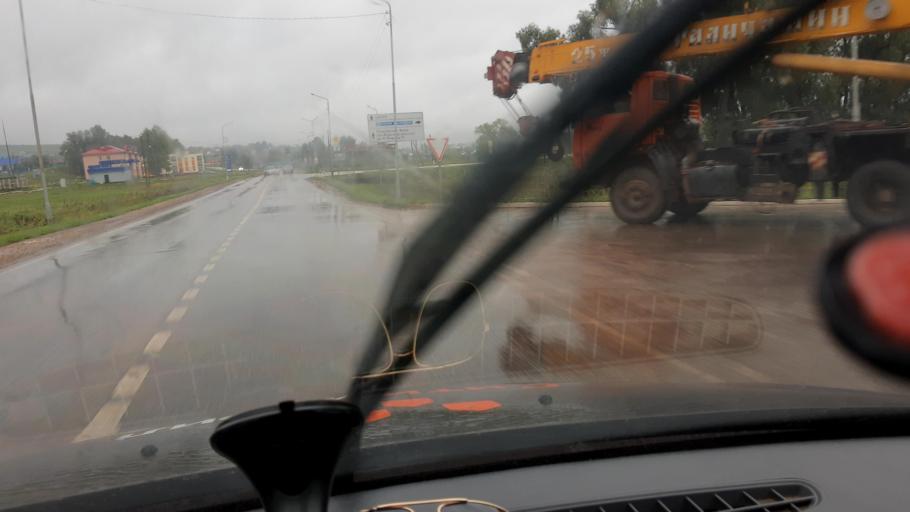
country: RU
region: Bashkortostan
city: Karmaskaly
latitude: 53.9123
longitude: 56.4405
